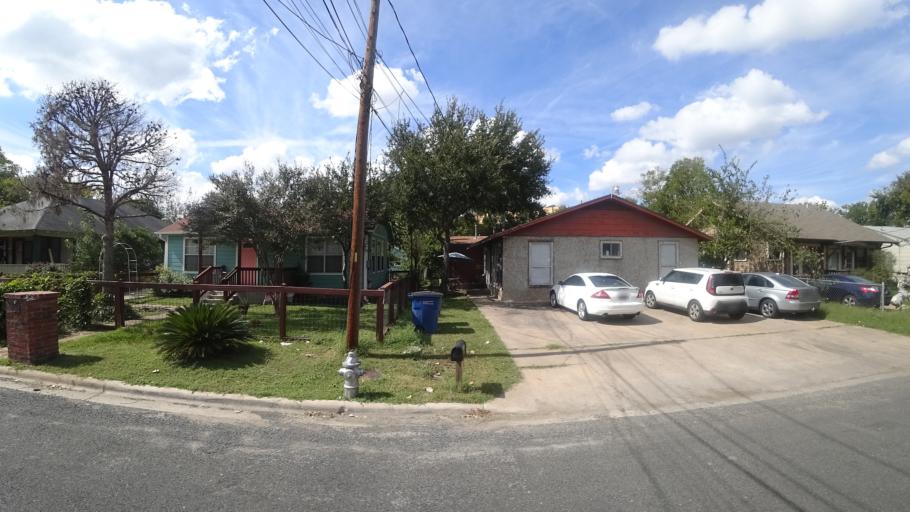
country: US
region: Texas
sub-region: Travis County
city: Austin
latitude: 30.2645
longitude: -97.7062
